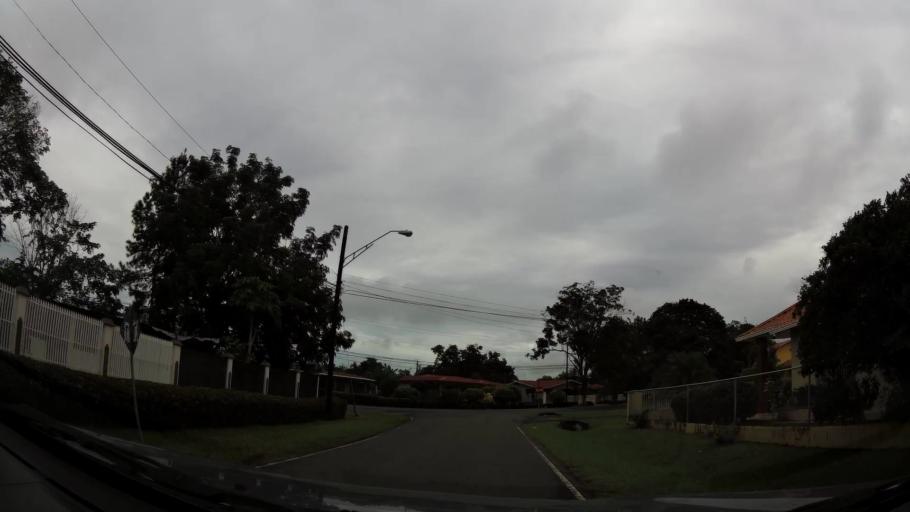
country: PA
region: Chiriqui
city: David
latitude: 8.4258
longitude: -82.4512
